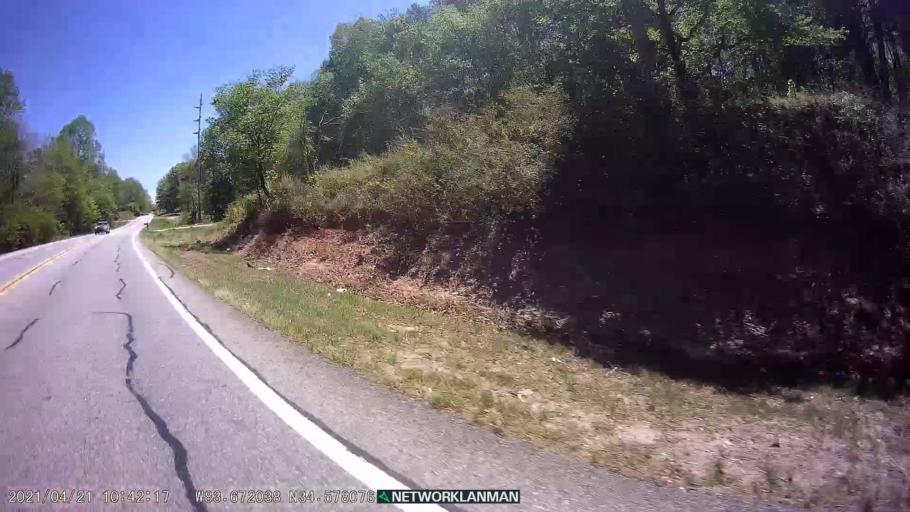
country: US
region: Georgia
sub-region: White County
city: Cleveland
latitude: 34.5780
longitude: -83.6716
